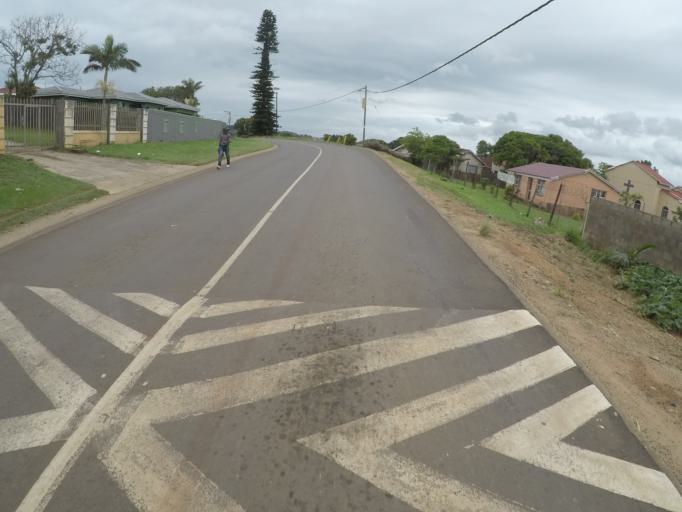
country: ZA
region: KwaZulu-Natal
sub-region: uThungulu District Municipality
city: Empangeni
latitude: -28.7708
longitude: 31.8647
